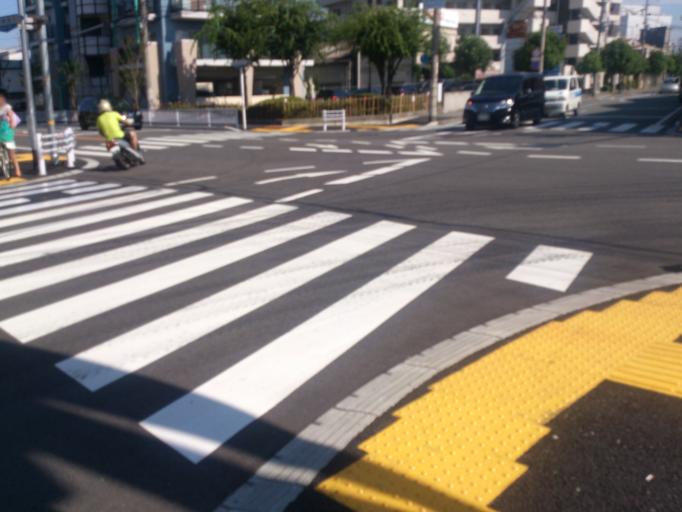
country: JP
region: Hyogo
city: Amagasaki
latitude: 34.7271
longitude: 135.4284
